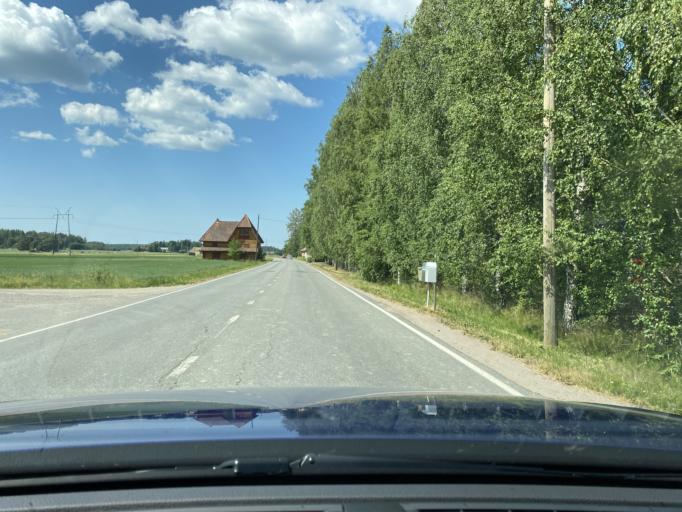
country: FI
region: Satakunta
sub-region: Rauma
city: Eura
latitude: 61.1440
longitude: 22.1144
